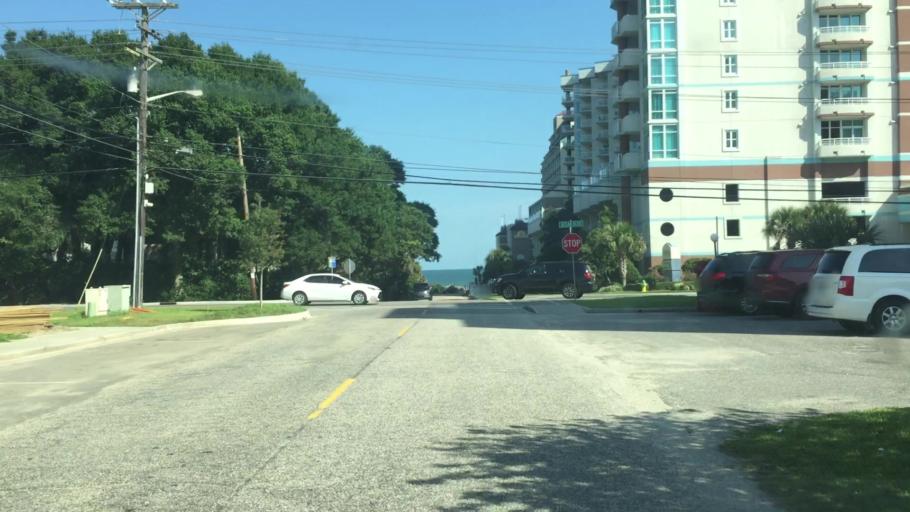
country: US
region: South Carolina
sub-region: Horry County
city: Myrtle Beach
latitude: 33.7455
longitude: -78.8156
